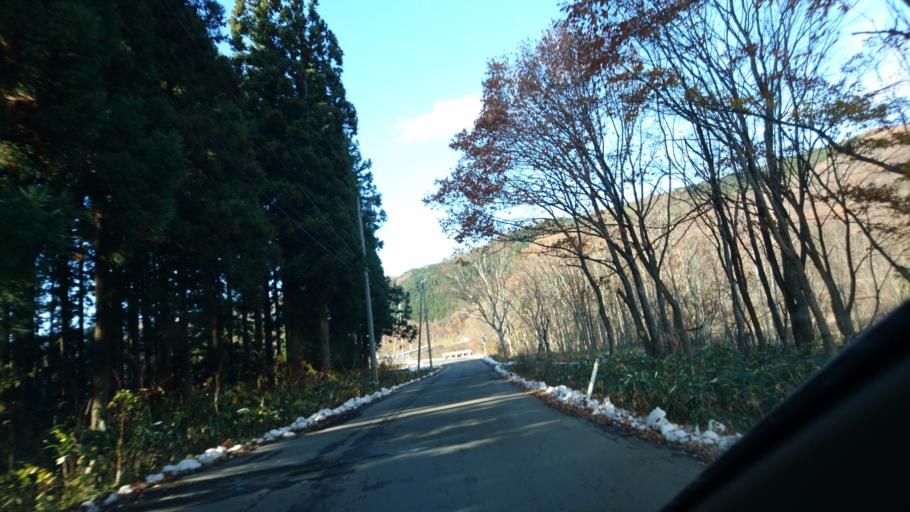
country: JP
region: Akita
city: Yokotemachi
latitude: 39.2987
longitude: 140.8295
